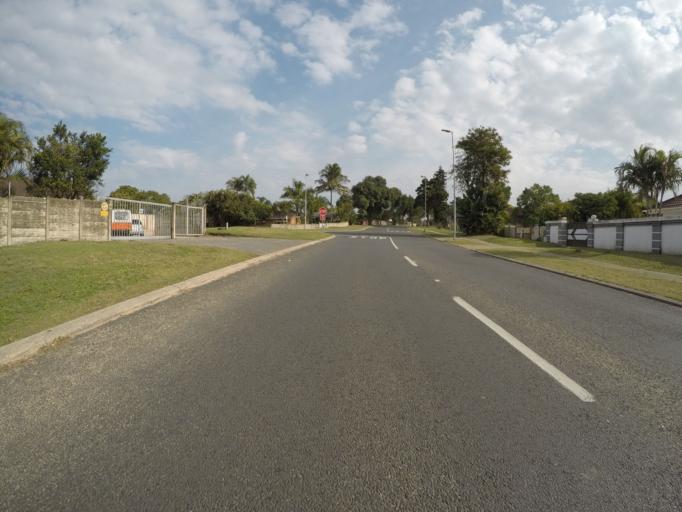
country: ZA
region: KwaZulu-Natal
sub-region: uThungulu District Municipality
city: Richards Bay
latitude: -28.7408
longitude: 32.0642
